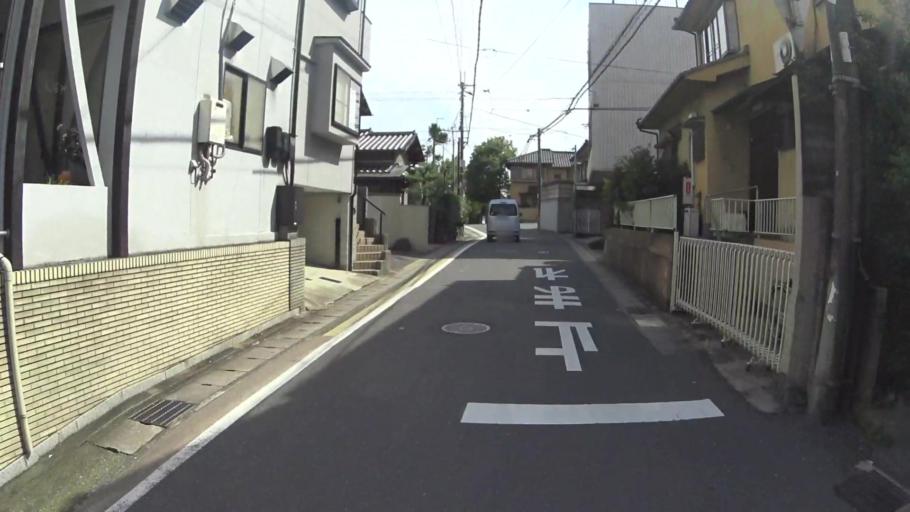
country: JP
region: Kyoto
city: Muko
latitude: 34.9825
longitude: 135.6884
